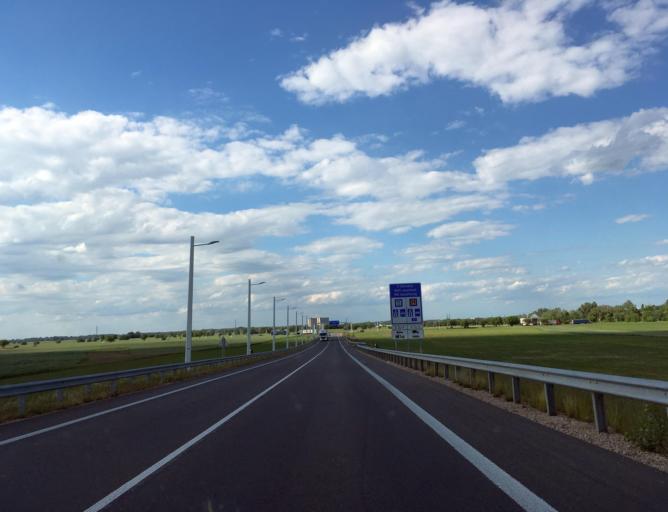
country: SK
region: Nitriansky
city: Komarno
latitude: 47.7609
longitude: 18.0846
